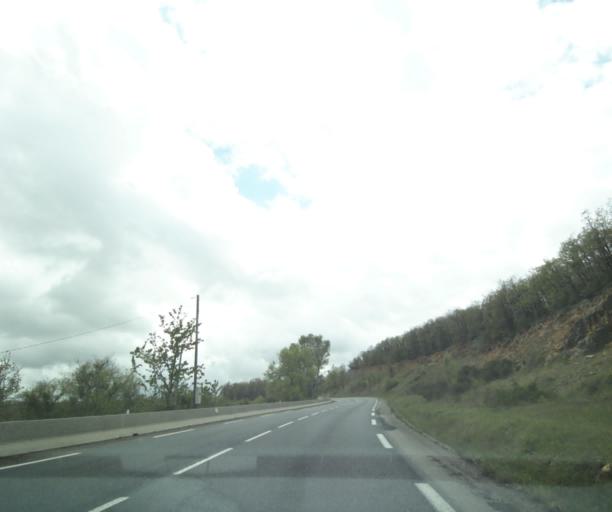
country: FR
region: Midi-Pyrenees
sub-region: Departement de l'Aveyron
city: Millau
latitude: 44.0847
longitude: 3.1262
